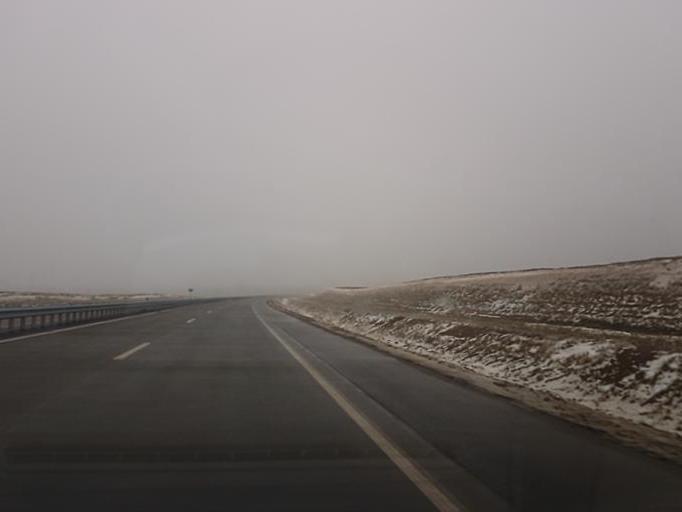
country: BY
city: Fanipol
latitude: 53.7630
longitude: 27.3832
